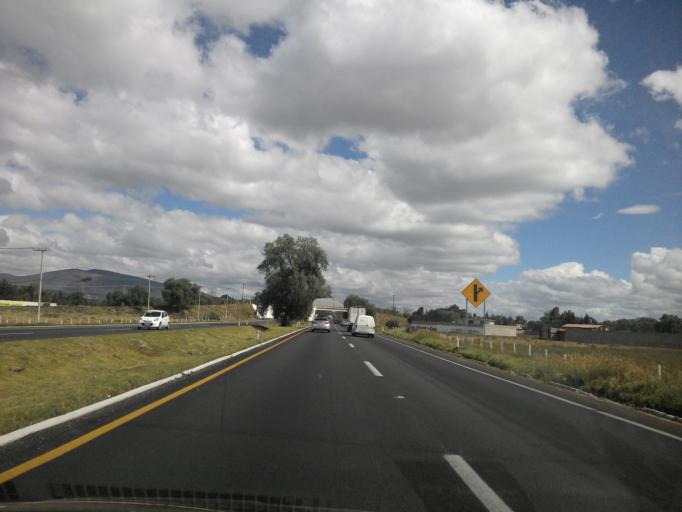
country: MX
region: Morelos
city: Xometla
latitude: 19.6465
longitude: -98.8904
